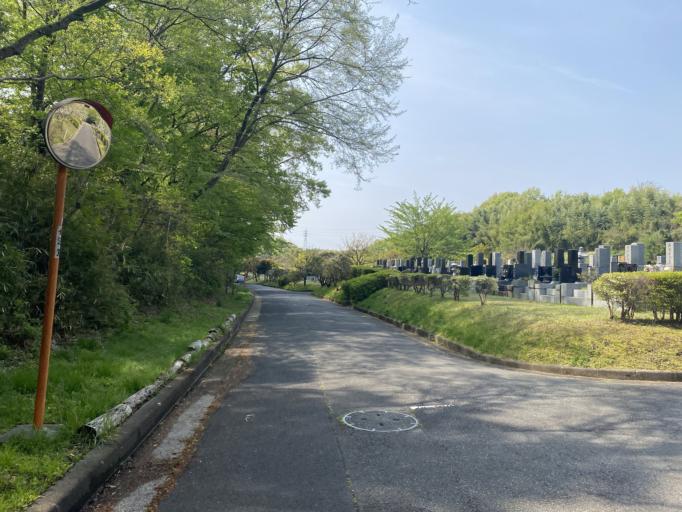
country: JP
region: Tokyo
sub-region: Machida-shi
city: Machida
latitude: 35.5745
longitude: 139.5192
